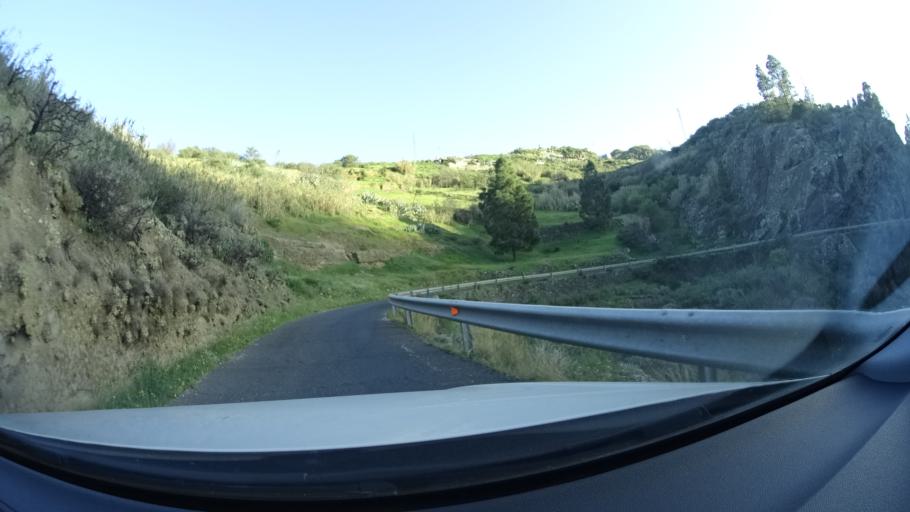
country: ES
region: Canary Islands
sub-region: Provincia de Las Palmas
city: Artenara
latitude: 28.0443
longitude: -15.6732
